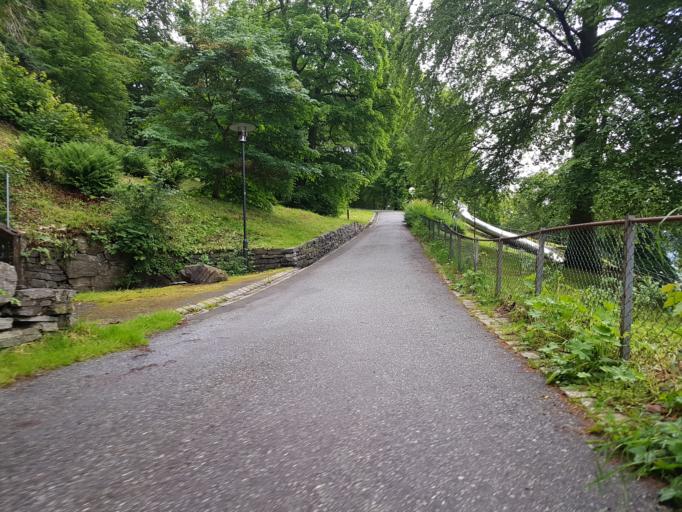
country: NO
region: Hordaland
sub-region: Bergen
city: Bergen
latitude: 60.3974
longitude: 5.3316
